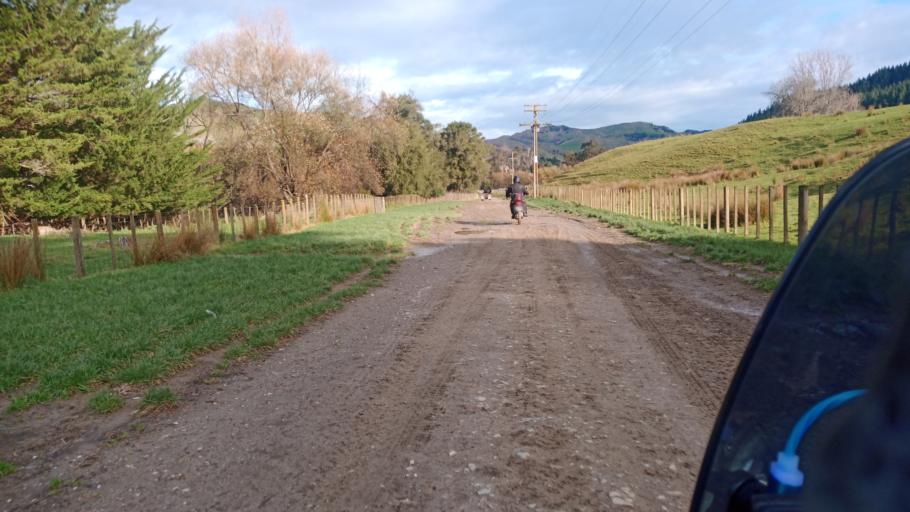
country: NZ
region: Gisborne
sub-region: Gisborne District
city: Gisborne
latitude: -38.3497
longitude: 177.9394
